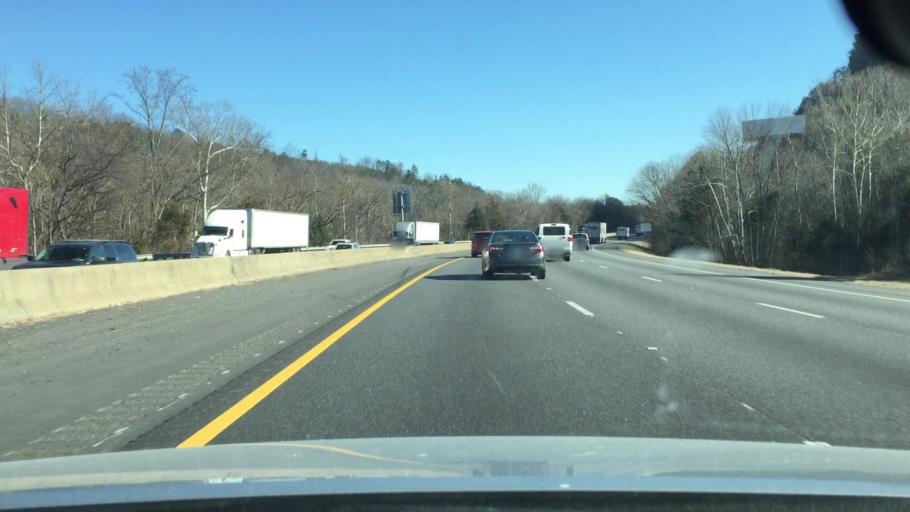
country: US
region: Georgia
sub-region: Catoosa County
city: Ringgold
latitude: 34.9087
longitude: -85.1080
